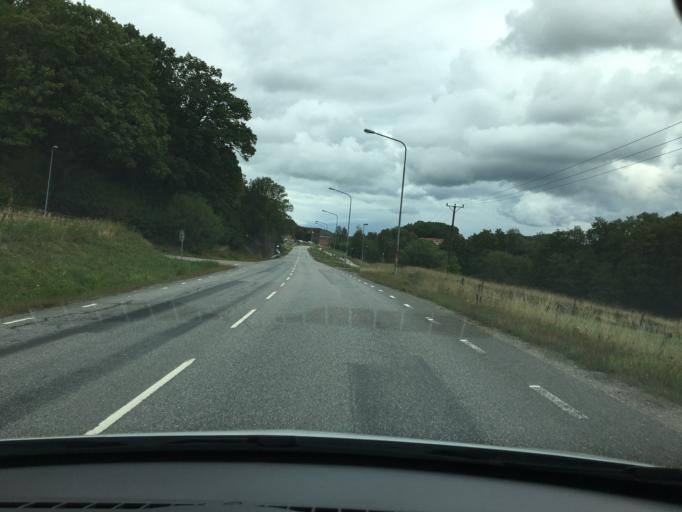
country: SE
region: Vaestra Goetaland
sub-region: Ale Kommun
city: Alafors
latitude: 57.9212
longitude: 12.0944
